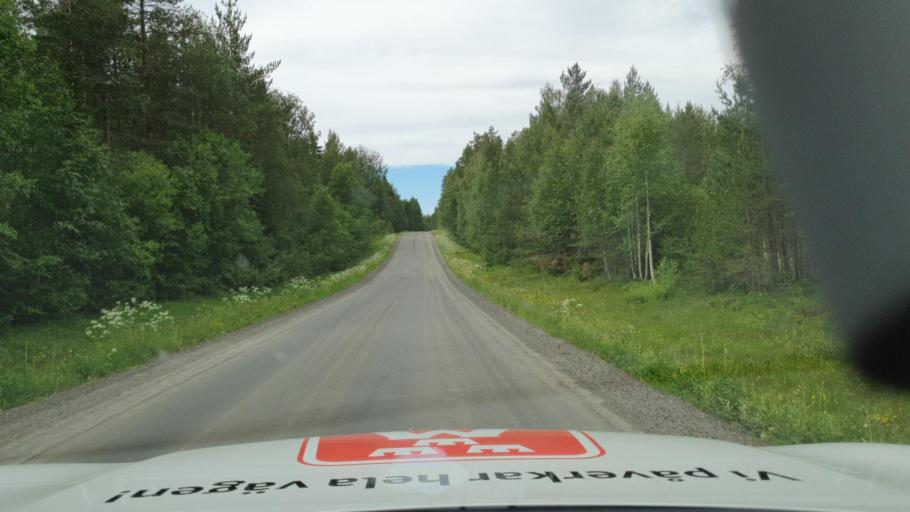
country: SE
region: Vaesterbotten
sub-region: Skelleftea Kommun
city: Burtraesk
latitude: 64.3687
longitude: 20.3910
